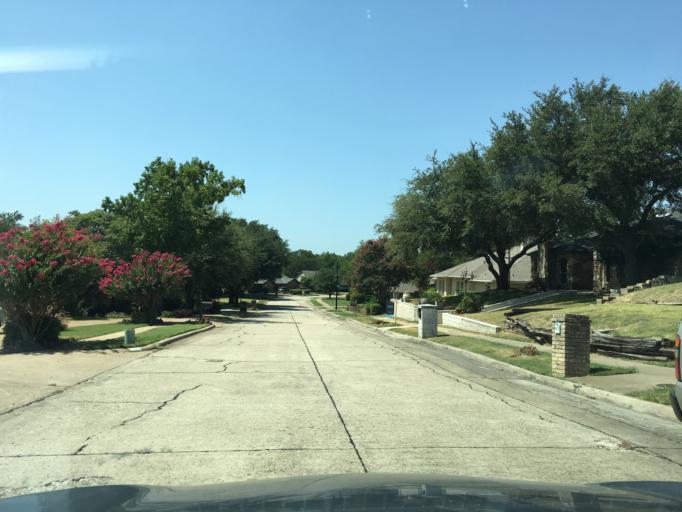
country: US
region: Texas
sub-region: Dallas County
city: Rowlett
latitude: 32.8856
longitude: -96.6024
